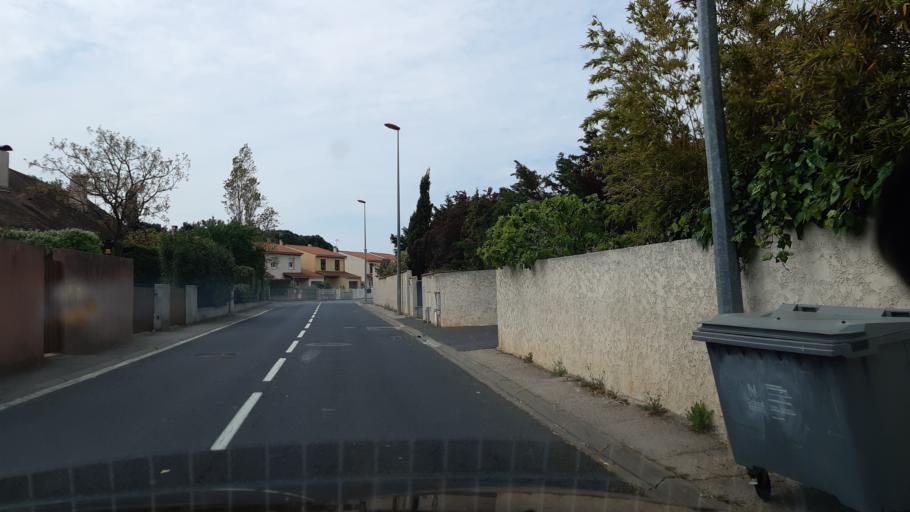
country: FR
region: Languedoc-Roussillon
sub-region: Departement de l'Aude
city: Narbonne
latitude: 43.1874
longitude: 3.0291
